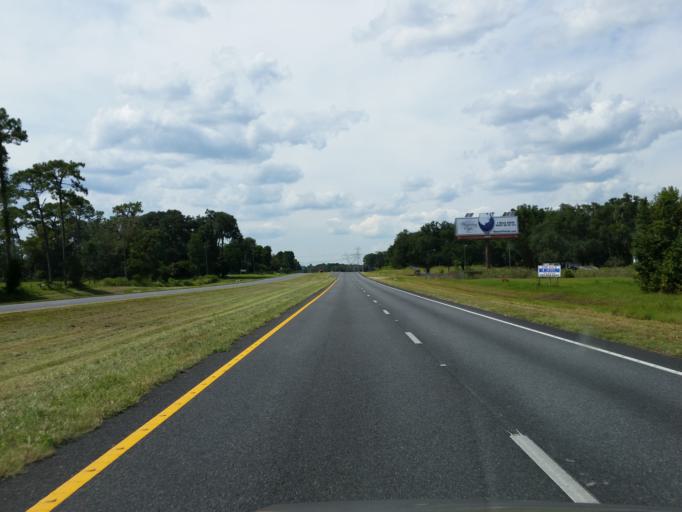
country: US
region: Florida
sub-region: Sumter County
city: Wildwood
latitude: 28.8631
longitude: -82.0765
